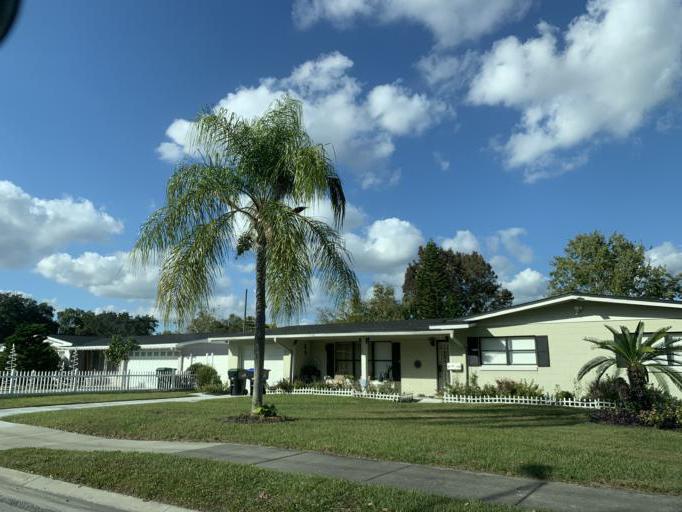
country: US
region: Florida
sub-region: Orange County
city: Fairview Shores
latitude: 28.6100
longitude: -81.4114
